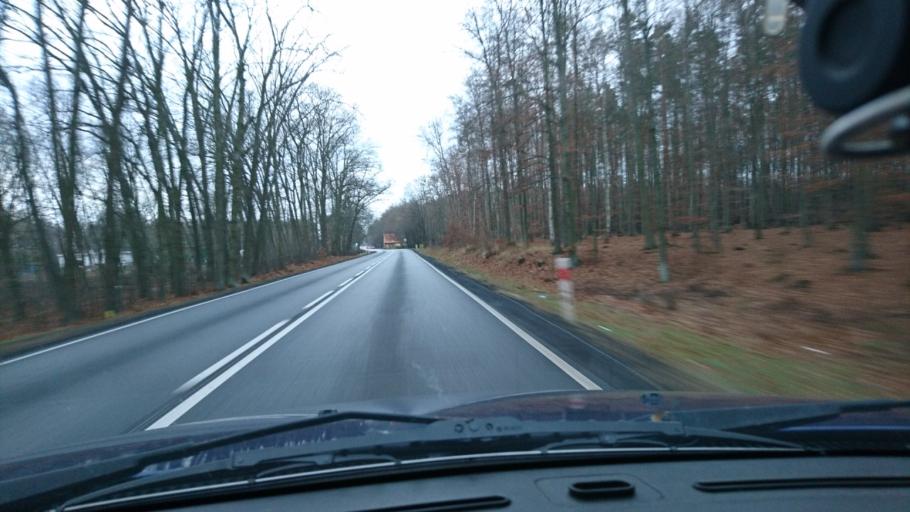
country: PL
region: Opole Voivodeship
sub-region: Powiat kluczborski
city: Kluczbork
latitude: 50.9640
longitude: 18.2815
